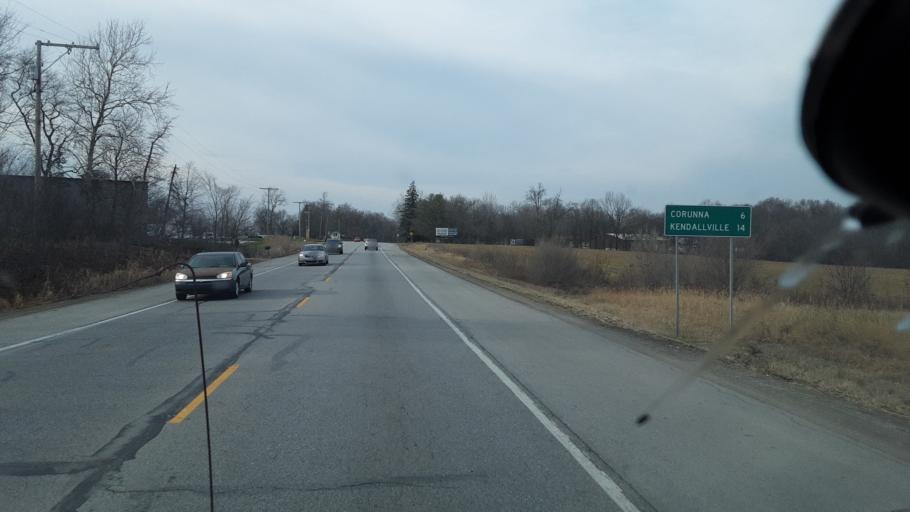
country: US
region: Indiana
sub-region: DeKalb County
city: Waterloo
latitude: 41.4342
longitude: -85.0280
